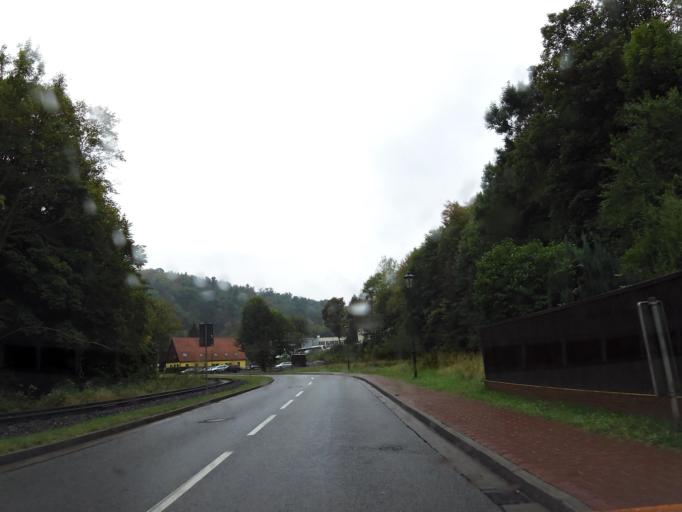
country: DE
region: Saxony-Anhalt
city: Harzgerode
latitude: 51.6523
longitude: 11.1171
